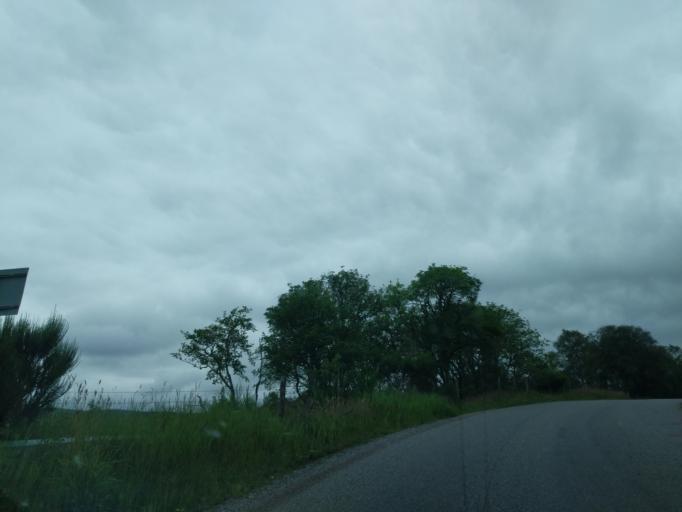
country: GB
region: Scotland
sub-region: Moray
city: Elgin
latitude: 57.5274
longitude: -3.4358
